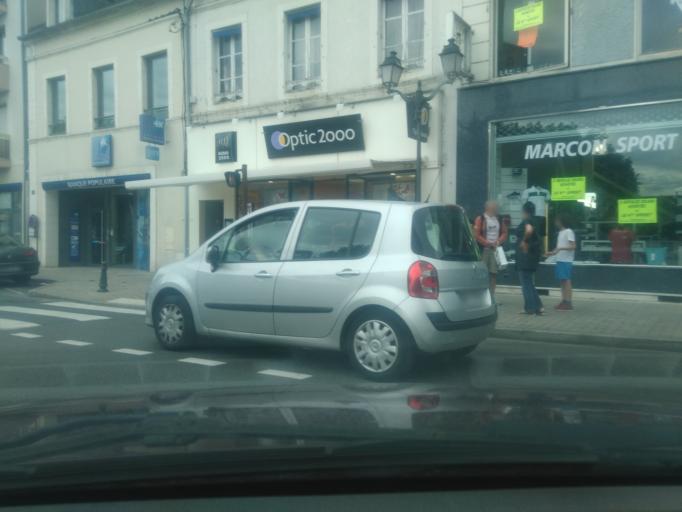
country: FR
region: Centre
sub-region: Departement du Cher
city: Saint-Amand-Montrond
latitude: 46.7224
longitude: 2.5047
